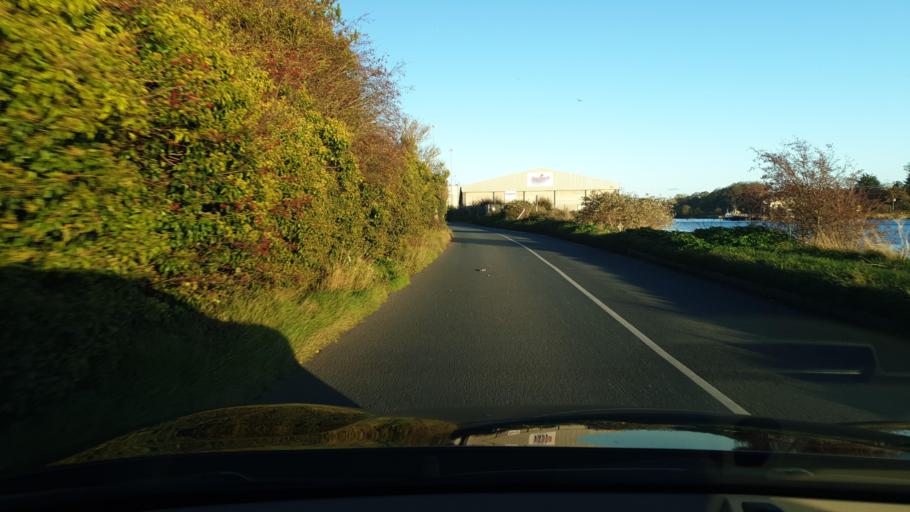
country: IE
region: Leinster
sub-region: Lu
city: Drogheda
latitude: 53.7211
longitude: -6.3132
